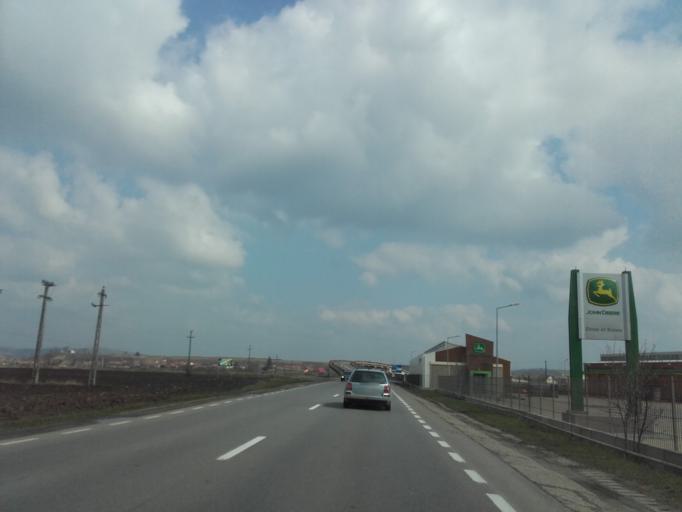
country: RO
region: Mures
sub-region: Comuna Sanpaul
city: Sanpaul
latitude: 46.4487
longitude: 24.3396
